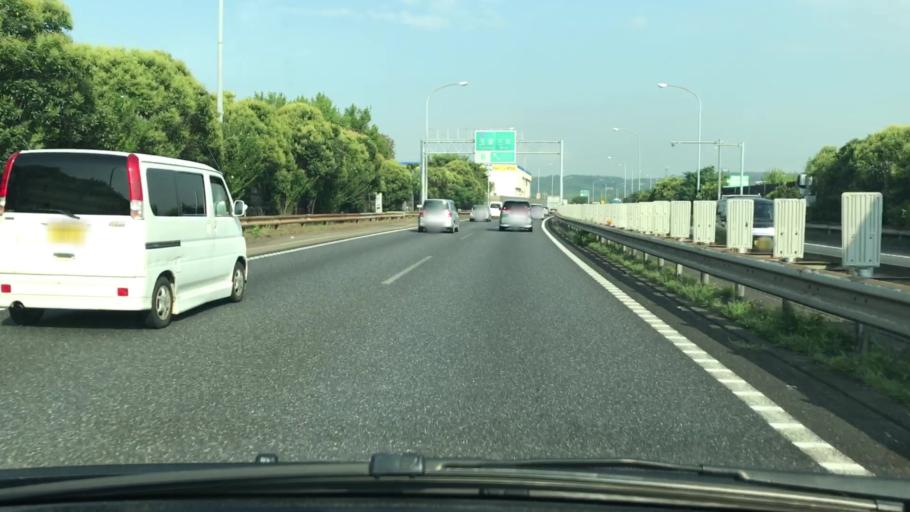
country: JP
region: Hyogo
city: Akashi
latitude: 34.6834
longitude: 134.9843
